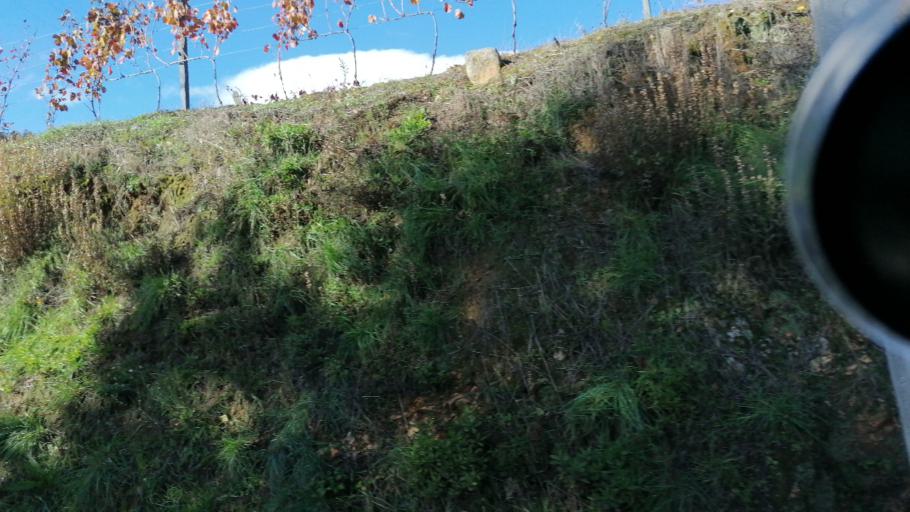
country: PT
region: Viseu
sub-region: Lamego
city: Lamego
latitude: 41.1200
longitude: -7.7948
